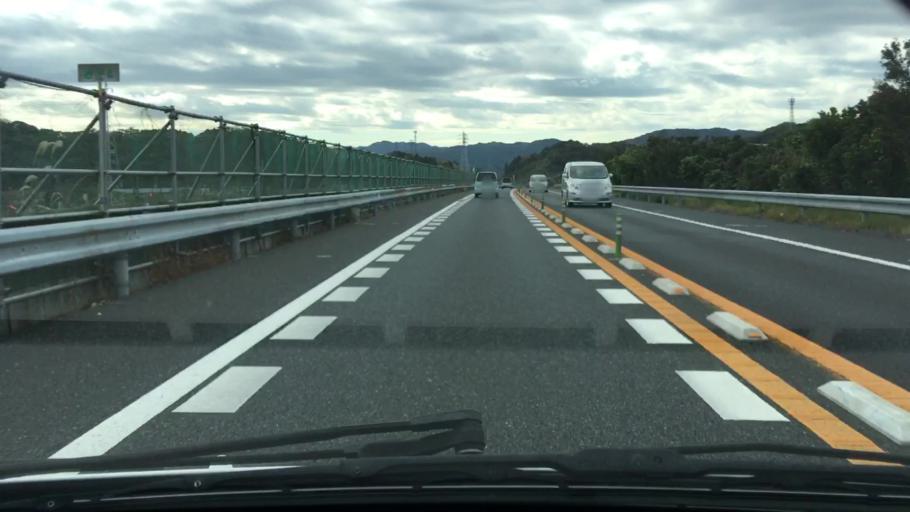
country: JP
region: Chiba
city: Kimitsu
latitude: 35.2363
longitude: 139.8880
